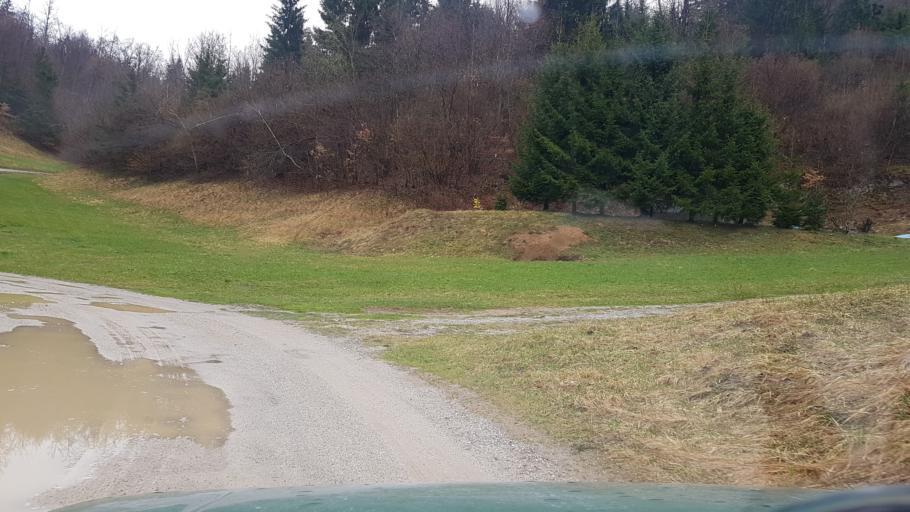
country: SI
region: Tolmin
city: Tolmin
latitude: 46.1358
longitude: 13.8494
